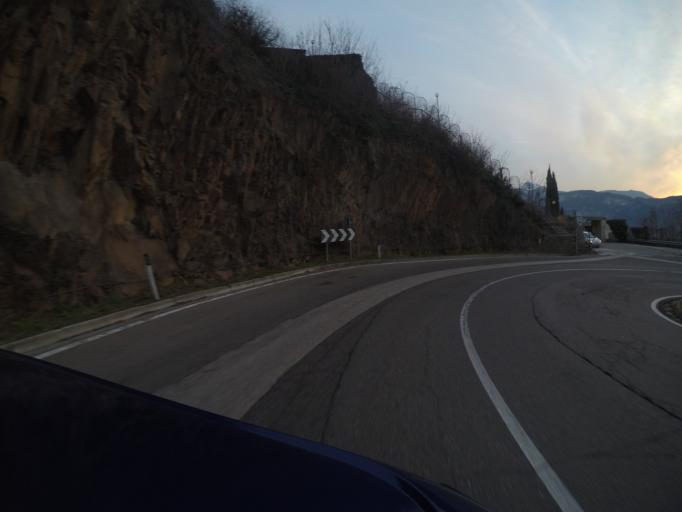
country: IT
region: Trentino-Alto Adige
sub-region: Provincia di Trento
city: Lavis
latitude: 46.1407
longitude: 11.1155
